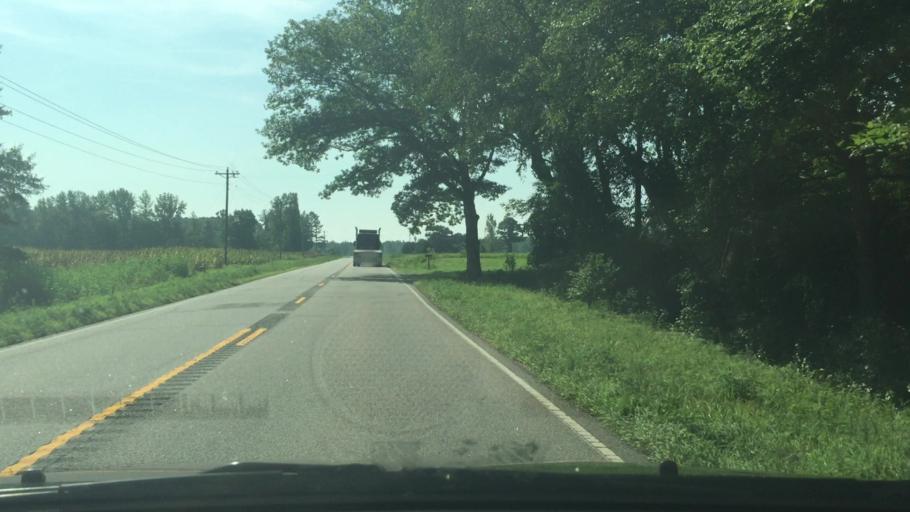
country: US
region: Virginia
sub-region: Sussex County
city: Sussex
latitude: 36.9948
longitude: -77.2593
